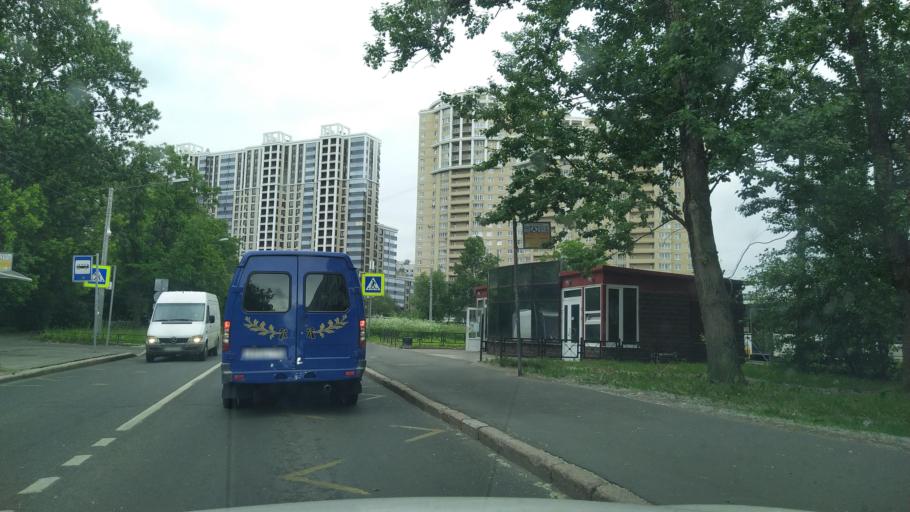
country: RU
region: St.-Petersburg
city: Kupchino
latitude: 59.8428
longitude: 30.3083
